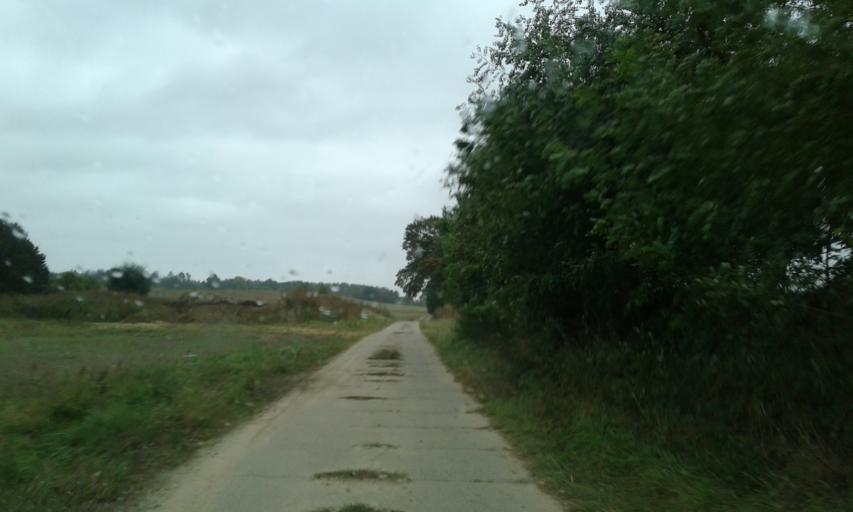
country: PL
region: West Pomeranian Voivodeship
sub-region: Powiat stargardzki
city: Dolice
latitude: 53.0997
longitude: 15.2177
